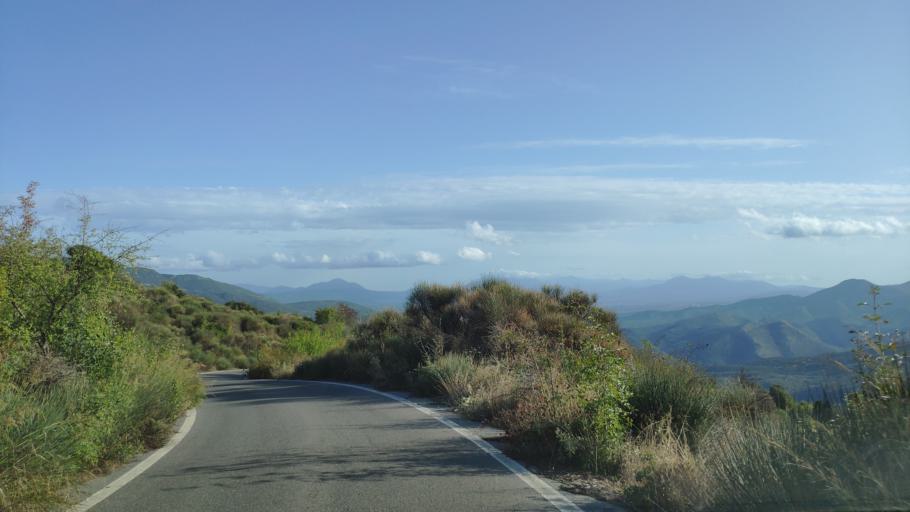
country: GR
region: Peloponnese
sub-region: Nomos Arkadias
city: Dimitsana
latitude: 37.5631
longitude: 22.0301
